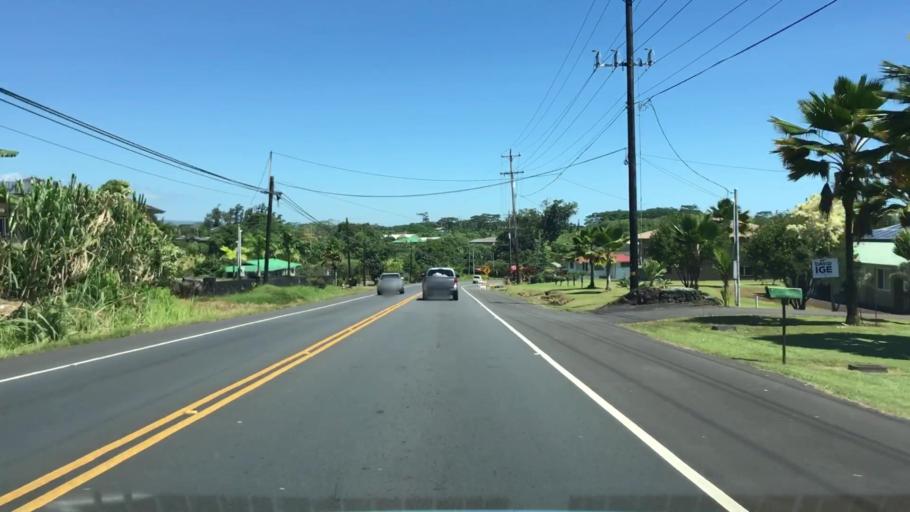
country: US
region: Hawaii
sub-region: Hawaii County
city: Kurtistown
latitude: 19.5866
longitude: -155.0607
